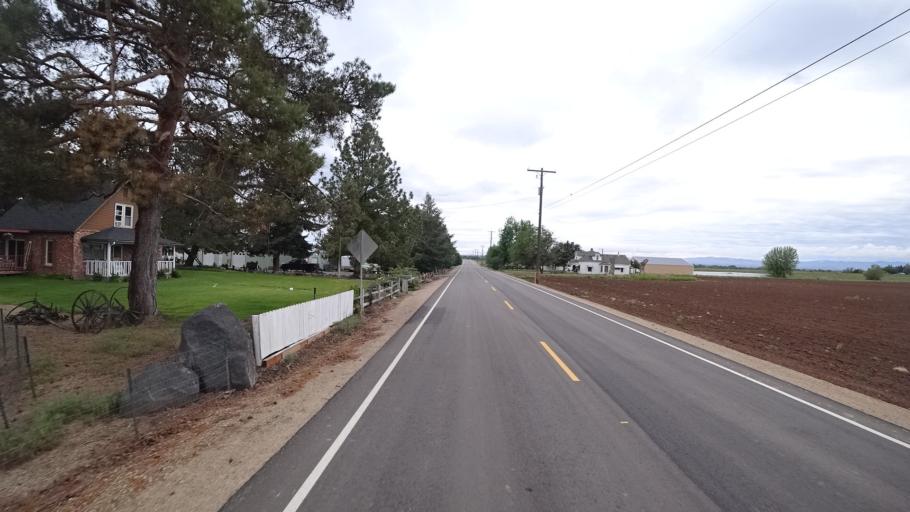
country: US
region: Idaho
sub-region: Ada County
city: Star
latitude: 43.6646
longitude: -116.5129
